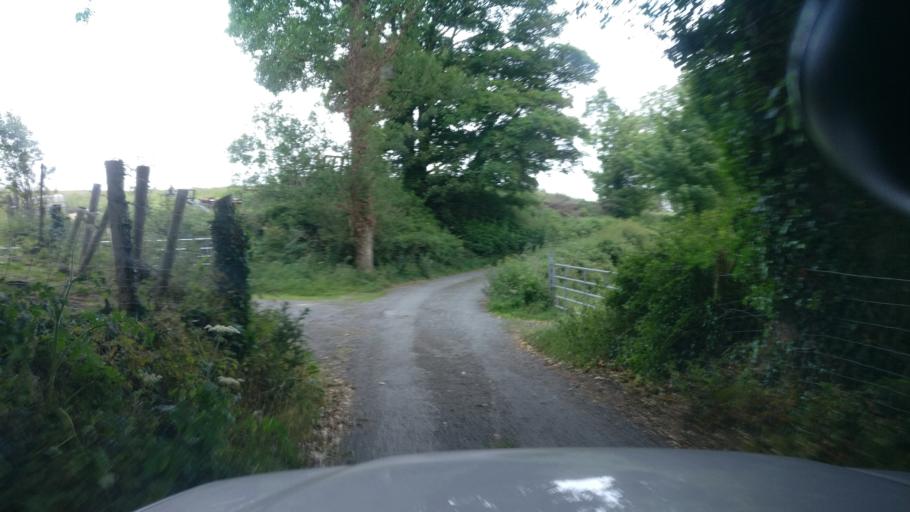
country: IE
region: Connaught
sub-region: County Galway
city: Ballinasloe
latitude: 53.2983
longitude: -8.2870
